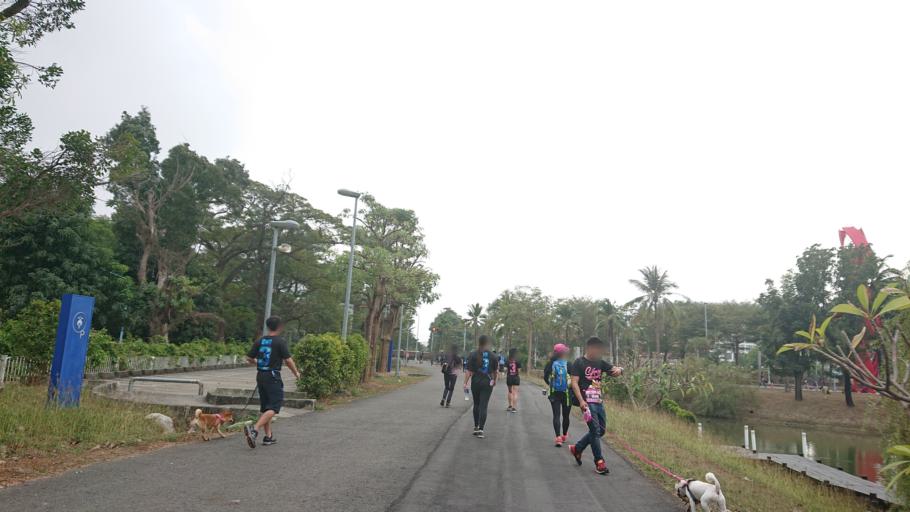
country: TW
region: Kaohsiung
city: Kaohsiung
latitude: 22.7018
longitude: 120.2971
